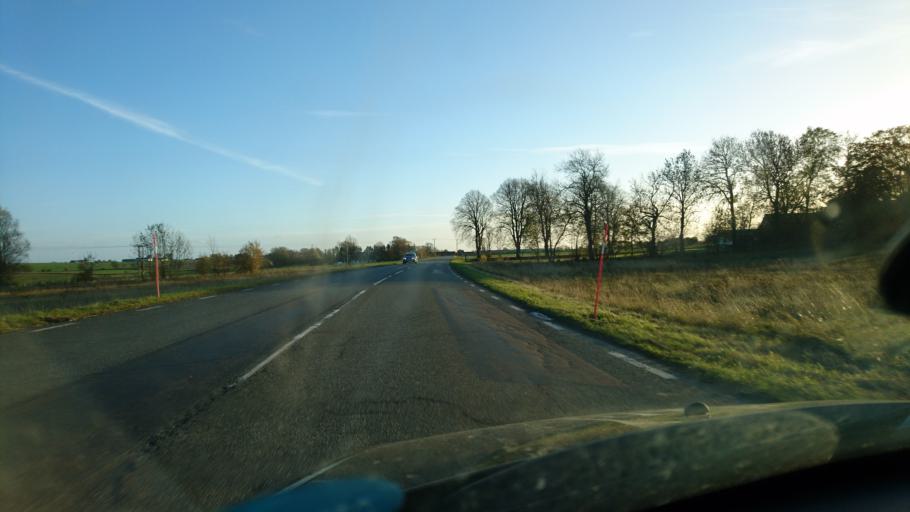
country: SE
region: Skane
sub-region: Simrishamns Kommun
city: Simrishamn
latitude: 55.4993
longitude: 14.1622
